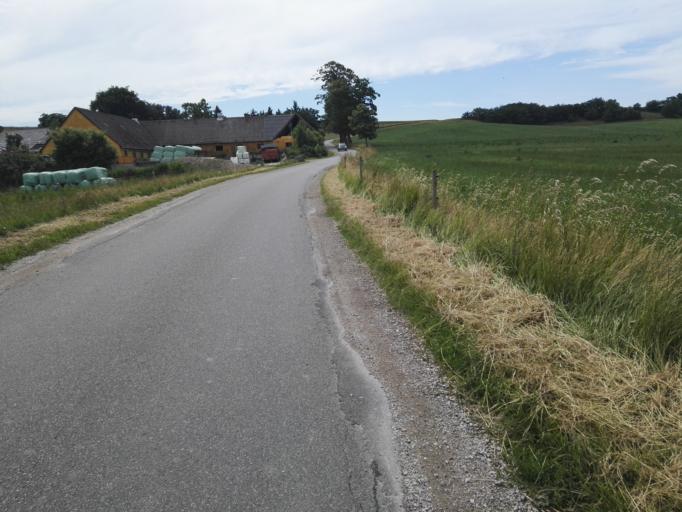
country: DK
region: Capital Region
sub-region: Hillerod Kommune
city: Skaevinge
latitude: 55.8922
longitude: 12.1395
